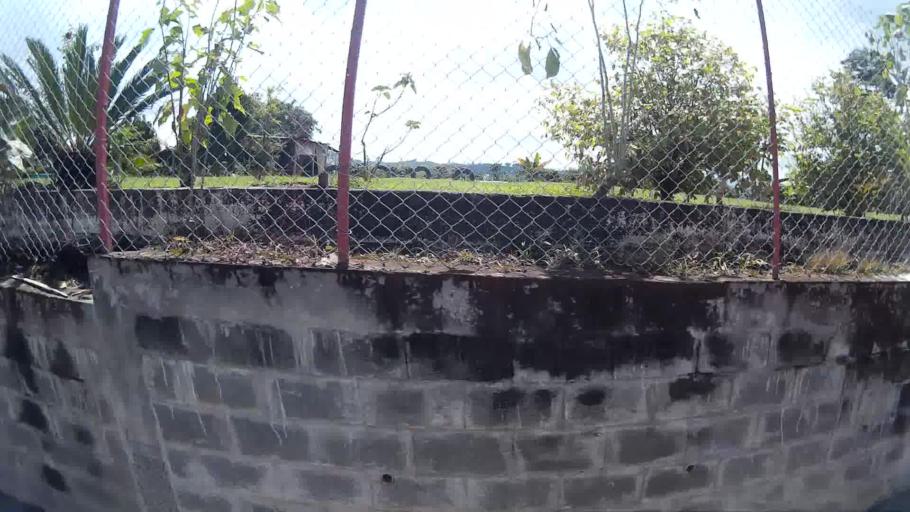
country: CO
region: Valle del Cauca
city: Ulloa
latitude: 4.7210
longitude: -75.7137
